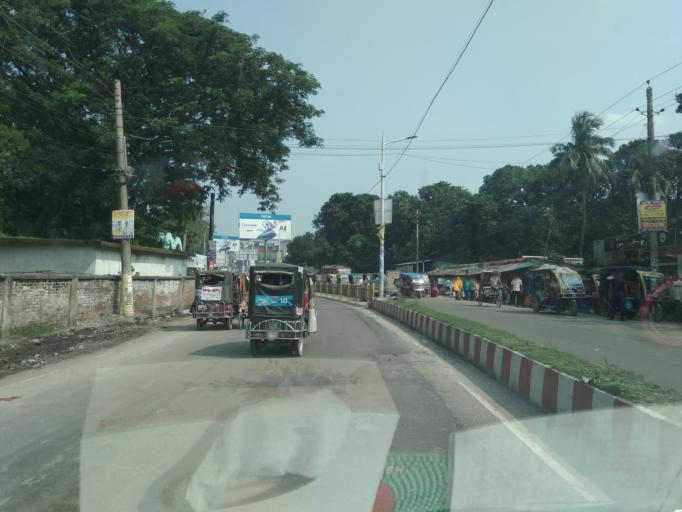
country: BD
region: Rangpur Division
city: Rangpur
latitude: 25.7669
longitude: 89.2302
